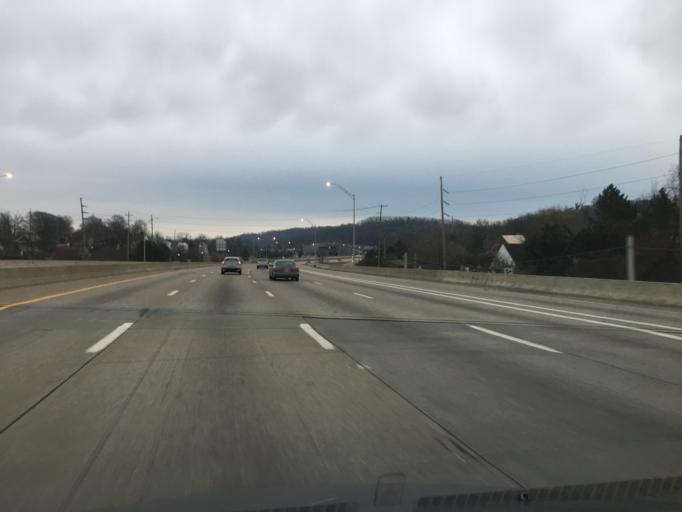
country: US
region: Kentucky
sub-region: Kenton County
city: Park Hills
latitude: 39.0780
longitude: -84.5208
